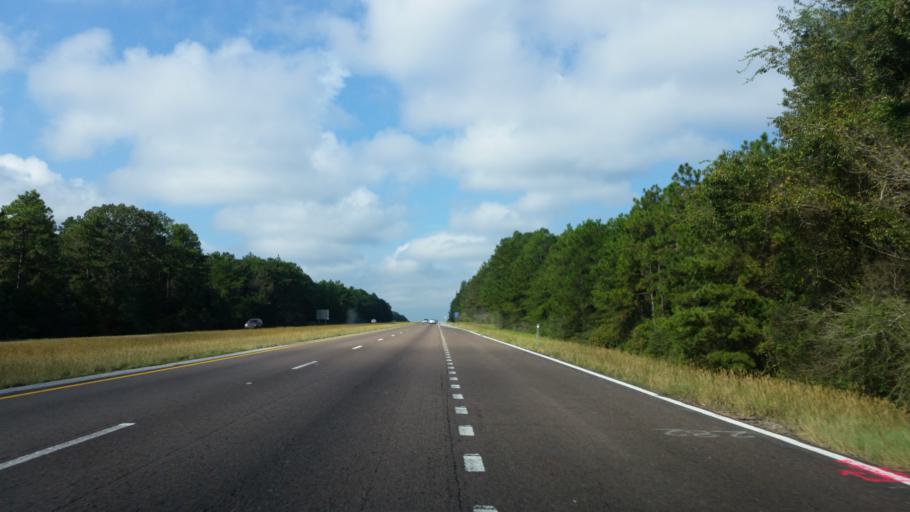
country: US
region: Alabama
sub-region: Baldwin County
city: Bay Minette
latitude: 30.9636
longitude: -87.7648
